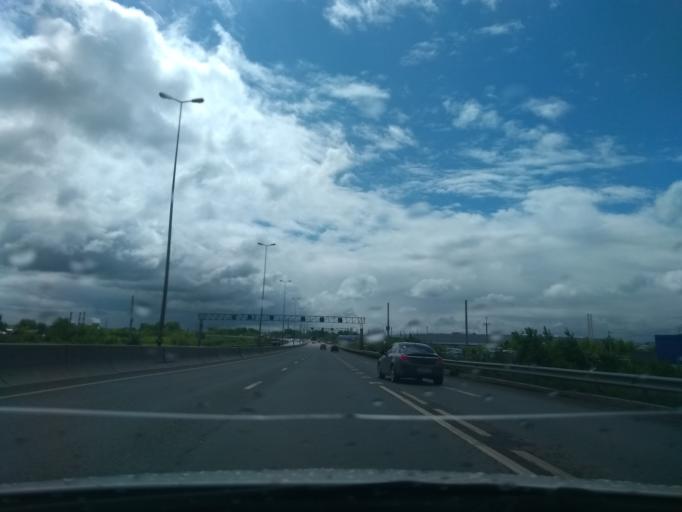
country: RU
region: Perm
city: Kondratovo
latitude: 57.9520
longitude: 56.1224
